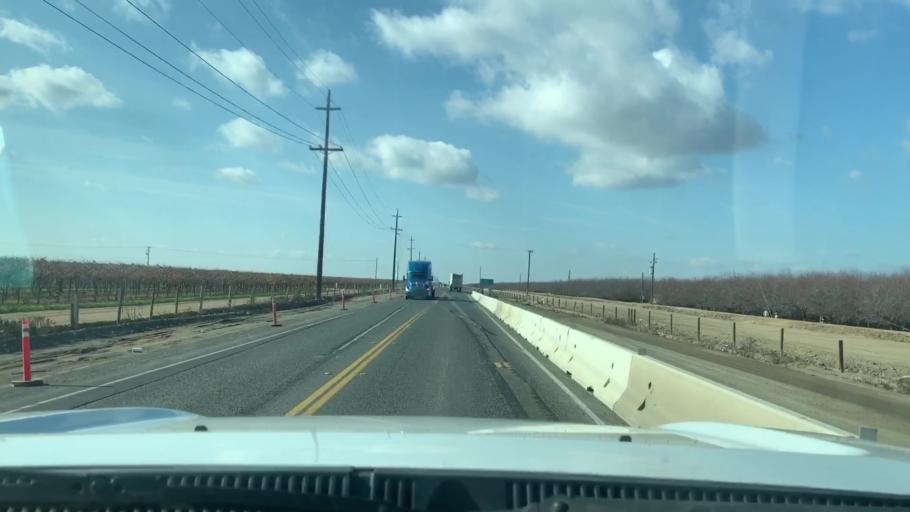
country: US
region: California
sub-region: Kern County
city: McFarland
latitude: 35.6020
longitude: -119.2196
